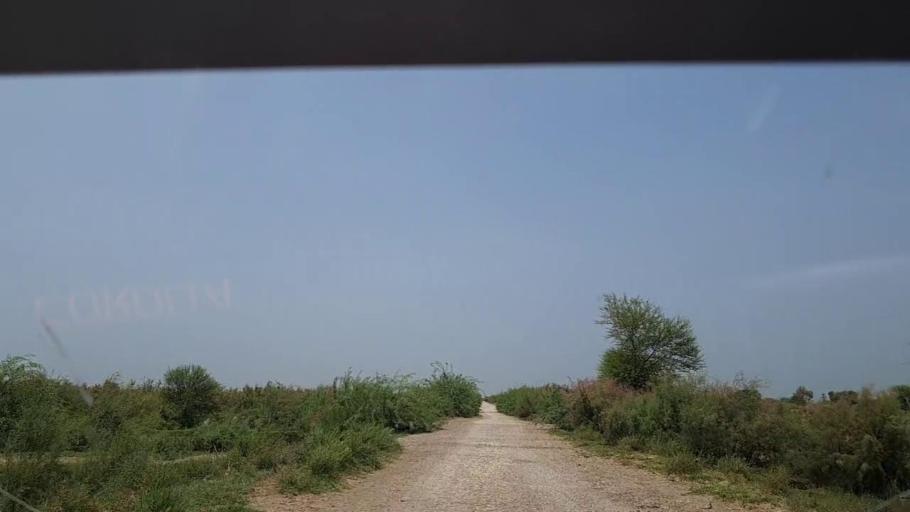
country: PK
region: Sindh
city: Adilpur
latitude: 27.8934
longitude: 69.2457
